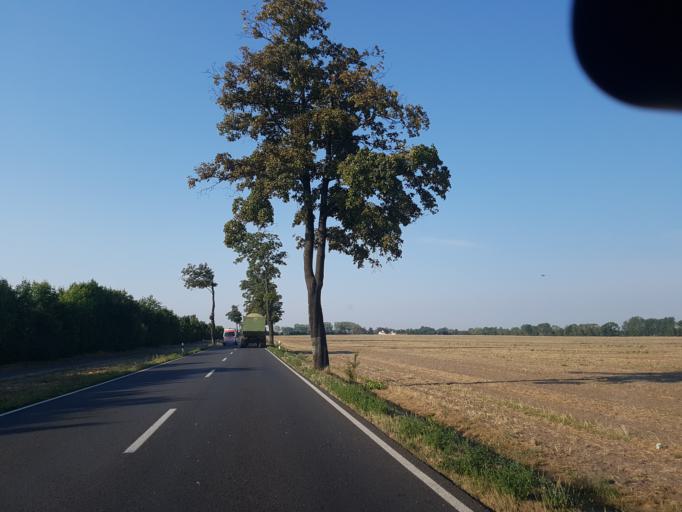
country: DE
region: Brandenburg
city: Elsterwerda
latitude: 51.4422
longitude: 13.5152
